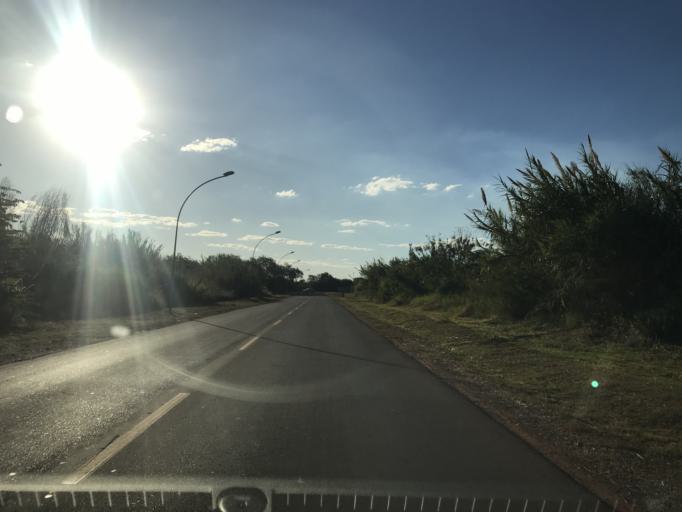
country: BR
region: Federal District
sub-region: Brasilia
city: Brasilia
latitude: -15.8088
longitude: -47.8421
